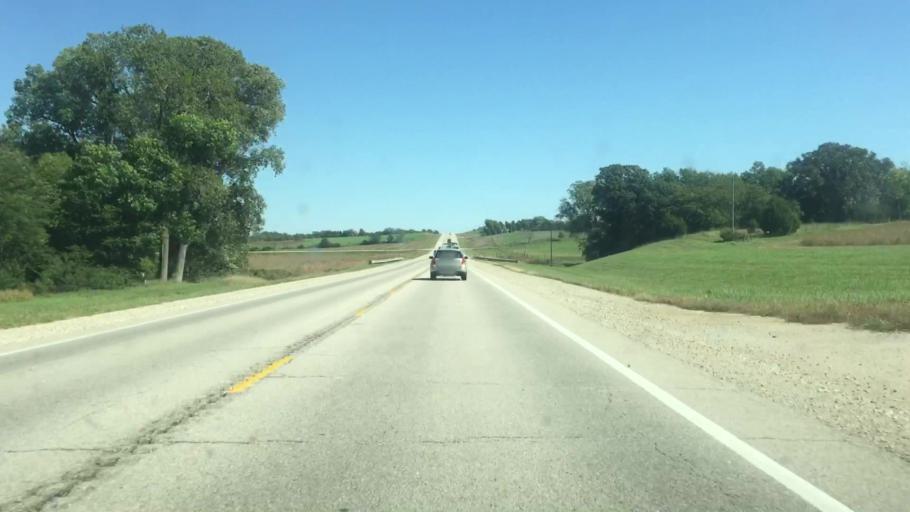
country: US
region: Kansas
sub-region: Nemaha County
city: Seneca
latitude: 39.8425
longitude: -96.0038
